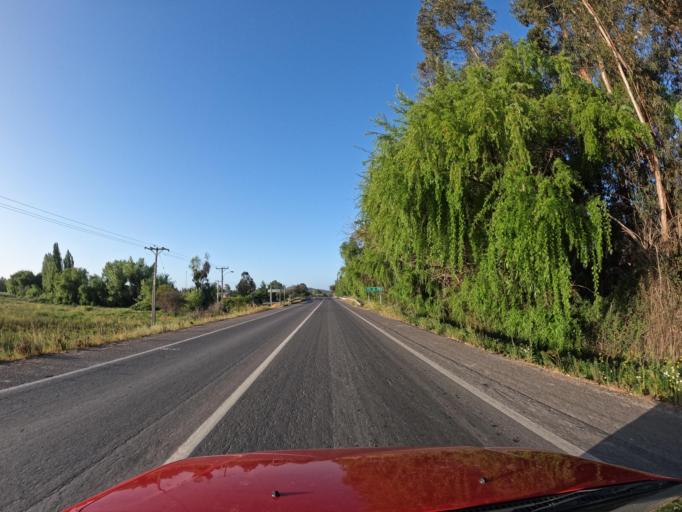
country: CL
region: O'Higgins
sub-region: Provincia de Colchagua
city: Santa Cruz
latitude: -34.3609
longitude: -71.4131
